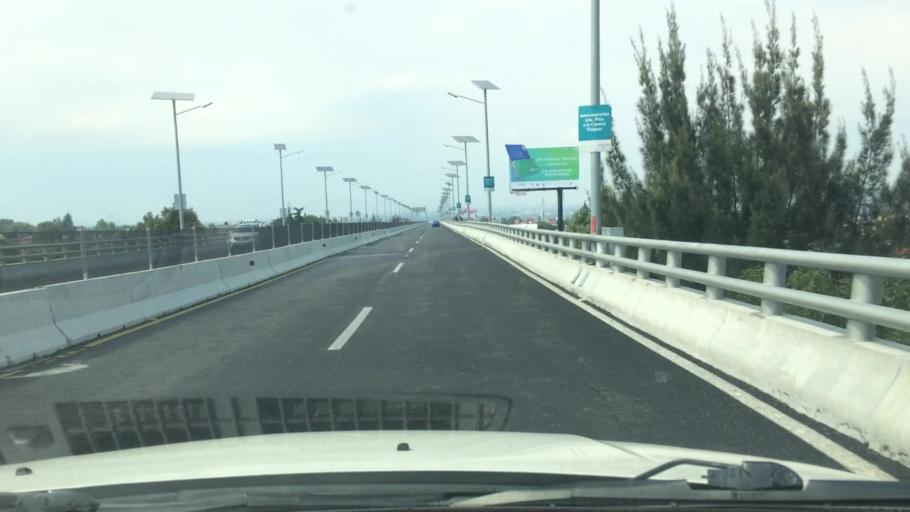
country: MX
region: Mexico City
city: Tlalpan
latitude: 19.2638
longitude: -99.1657
